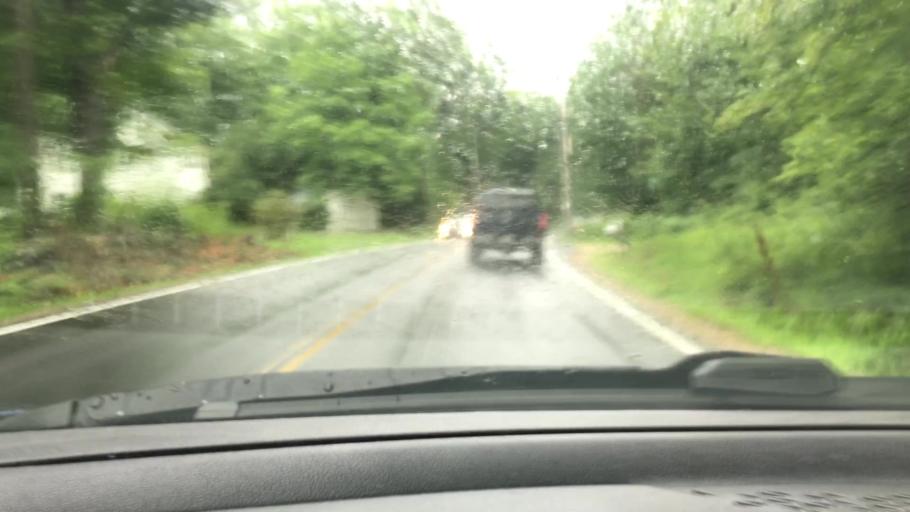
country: US
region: New Hampshire
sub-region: Rockingham County
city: Candia
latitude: 43.1653
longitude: -71.2459
